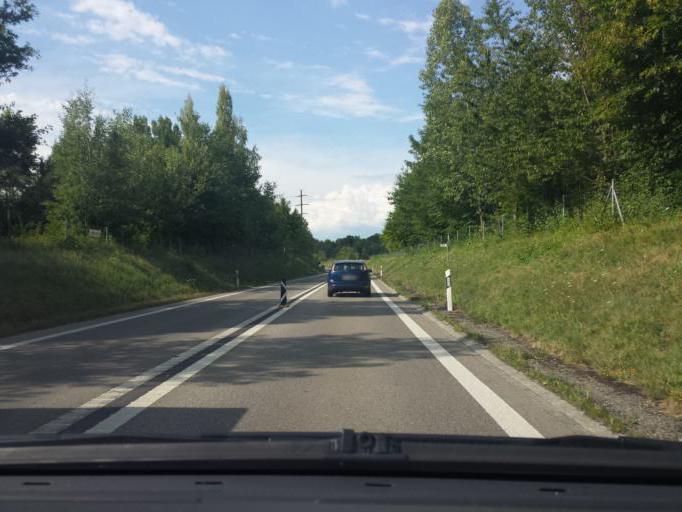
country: CH
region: Thurgau
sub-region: Arbon District
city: Roggwil
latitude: 47.5124
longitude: 9.4040
